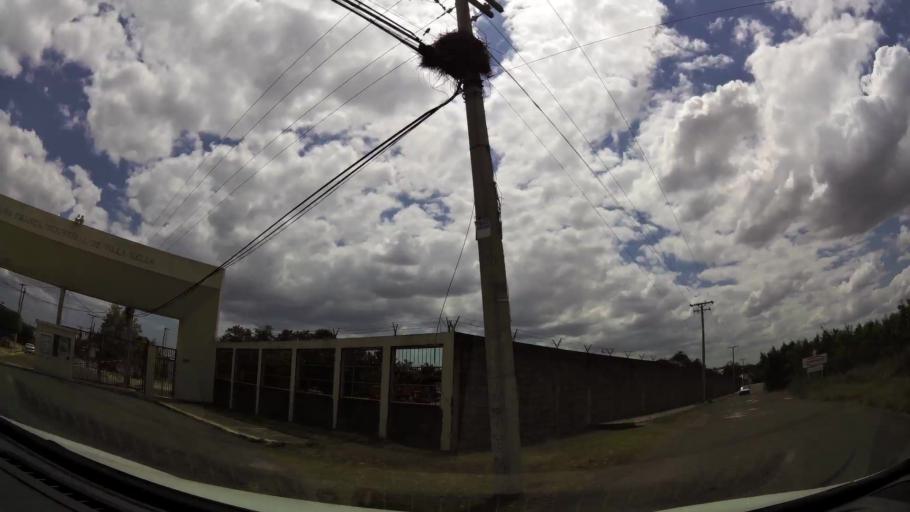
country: DO
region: Nacional
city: Ensanche Luperon
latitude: 18.5235
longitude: -69.9029
